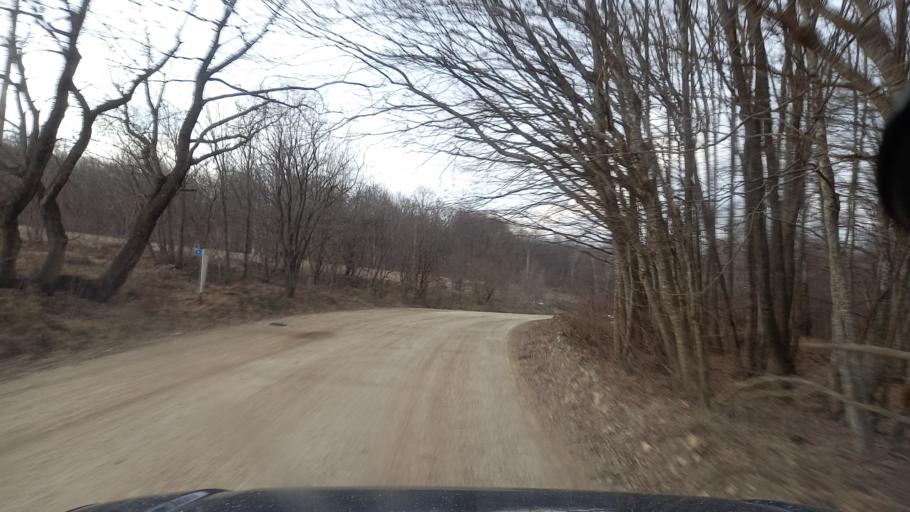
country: RU
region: Adygeya
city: Kamennomostskiy
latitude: 44.1474
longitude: 40.2491
